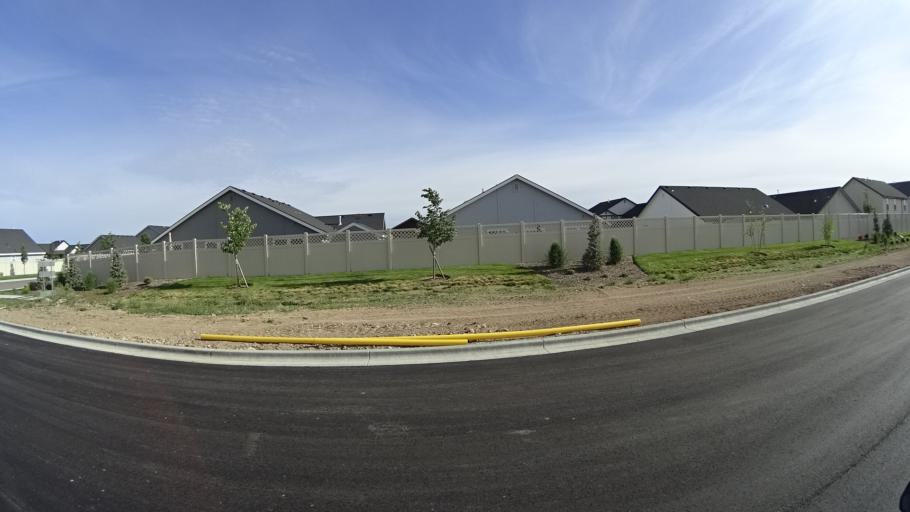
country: US
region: Idaho
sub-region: Ada County
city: Kuna
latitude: 43.5101
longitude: -116.4012
